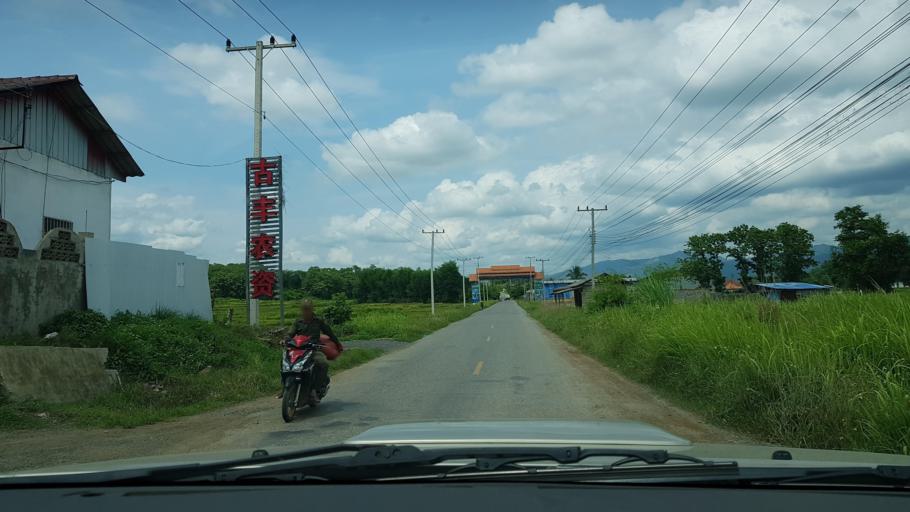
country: LA
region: Loungnamtha
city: Muang Nale
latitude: 20.1195
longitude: 101.4232
